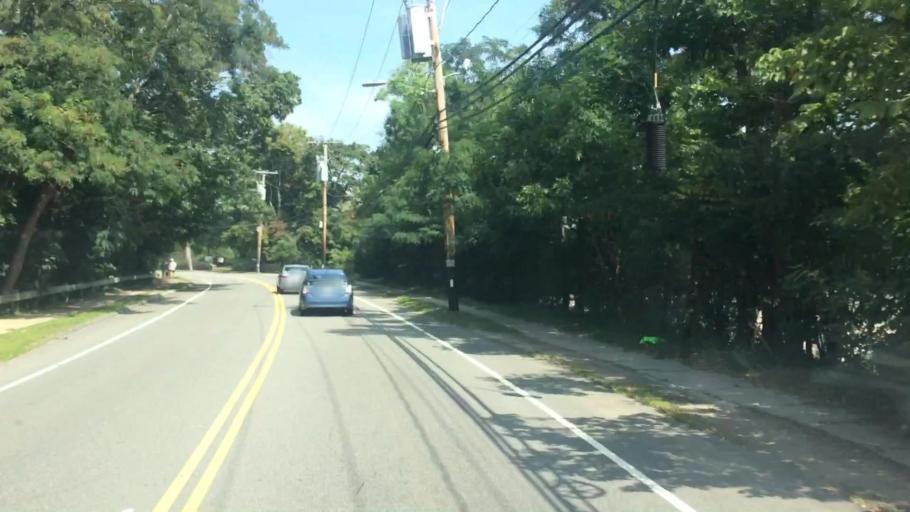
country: US
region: Massachusetts
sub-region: Norfolk County
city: Dedham
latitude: 42.2499
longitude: -71.1760
